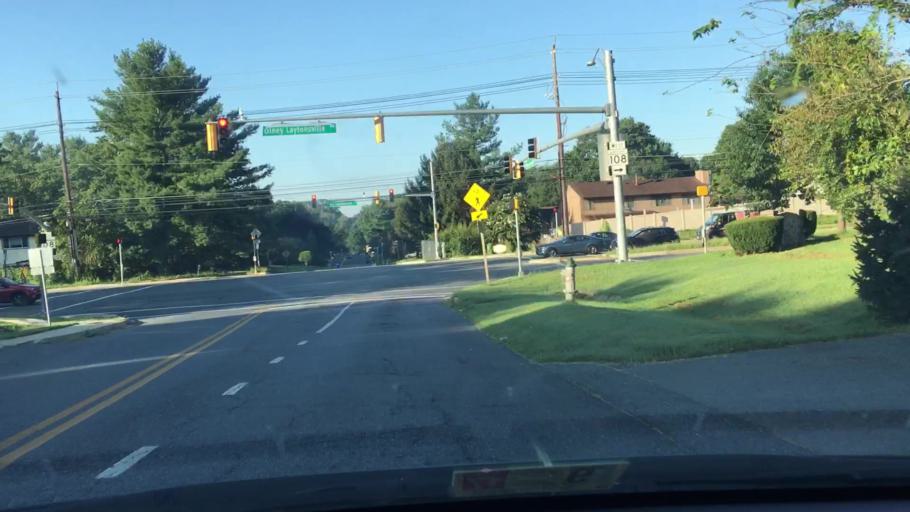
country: US
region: Maryland
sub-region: Montgomery County
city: Olney
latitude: 39.1600
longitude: -77.0771
